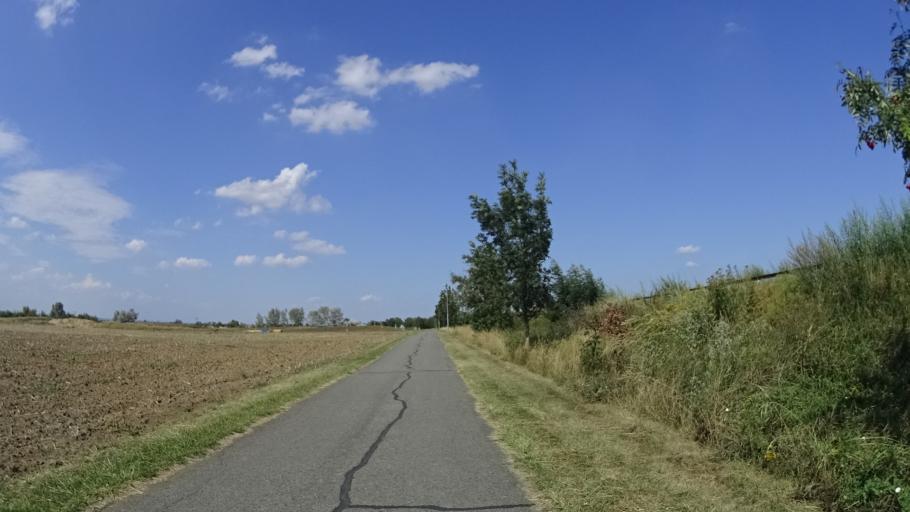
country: CZ
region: Zlin
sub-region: Okres Zlin
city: Ostrozska Nova Ves
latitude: 48.9978
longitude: 17.4219
